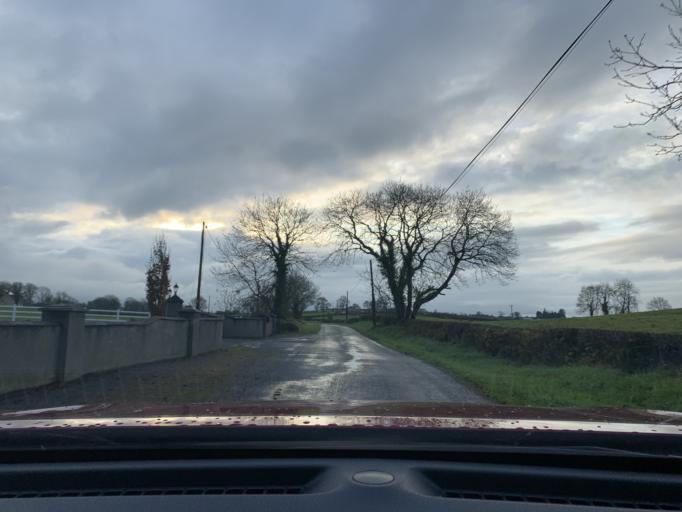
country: IE
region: Connaught
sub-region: Sligo
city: Ballymote
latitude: 54.0389
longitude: -8.5493
